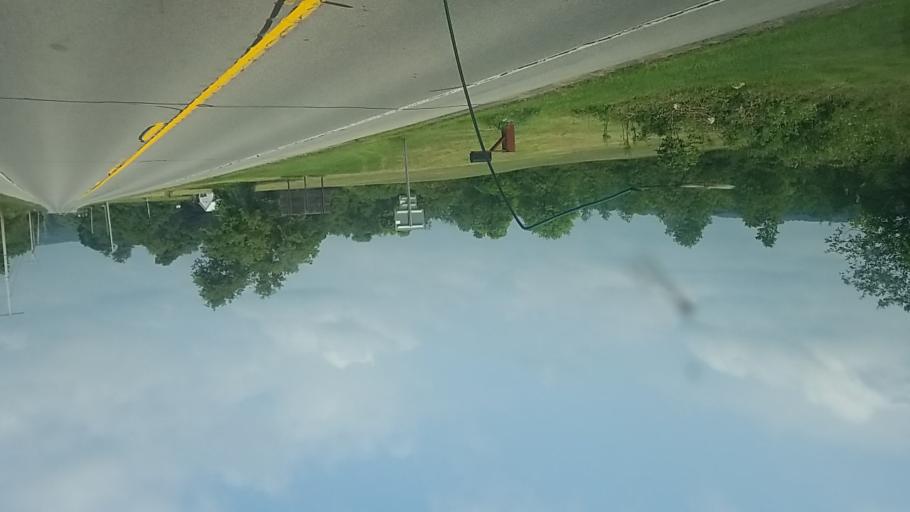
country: US
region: New York
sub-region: Montgomery County
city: Saint Johnsville
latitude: 42.9866
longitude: -74.6489
